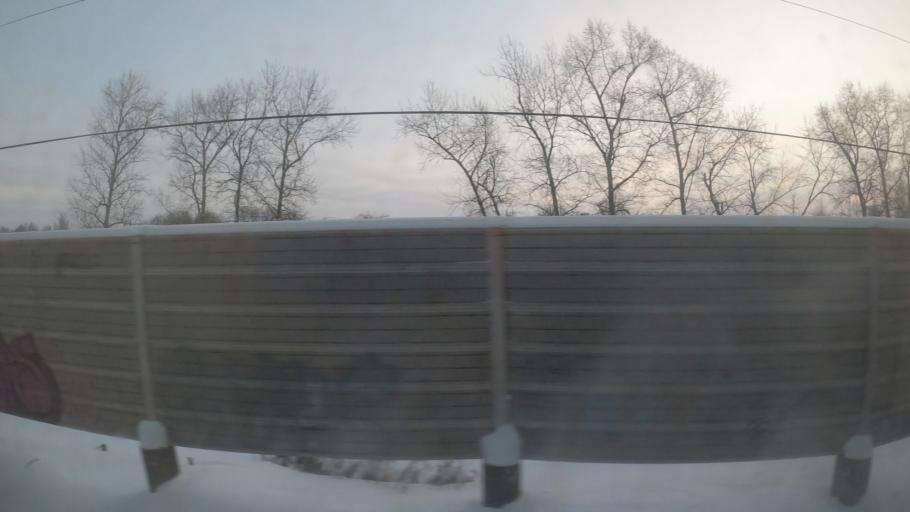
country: RU
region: Moskovskaya
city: Lobnya
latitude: 55.9981
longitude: 37.4922
